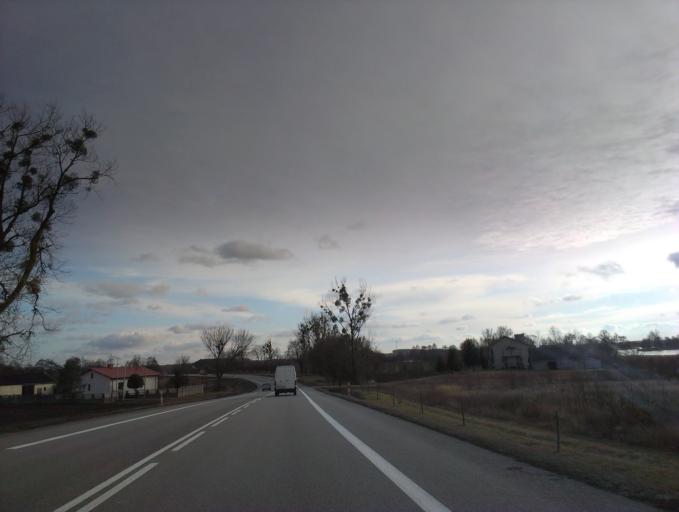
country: PL
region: Kujawsko-Pomorskie
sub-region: Powiat lipnowski
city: Kikol
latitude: 52.9211
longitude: 19.0959
